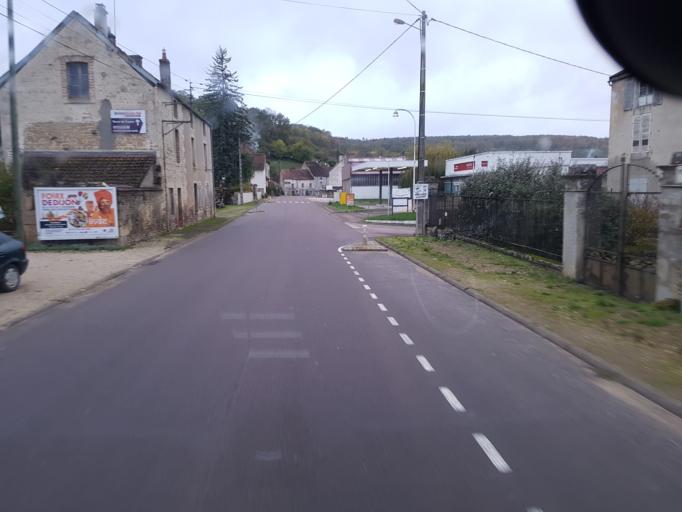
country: FR
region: Bourgogne
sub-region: Departement de la Cote-d'Or
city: Chatillon-sur-Seine
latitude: 47.6993
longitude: 4.6077
